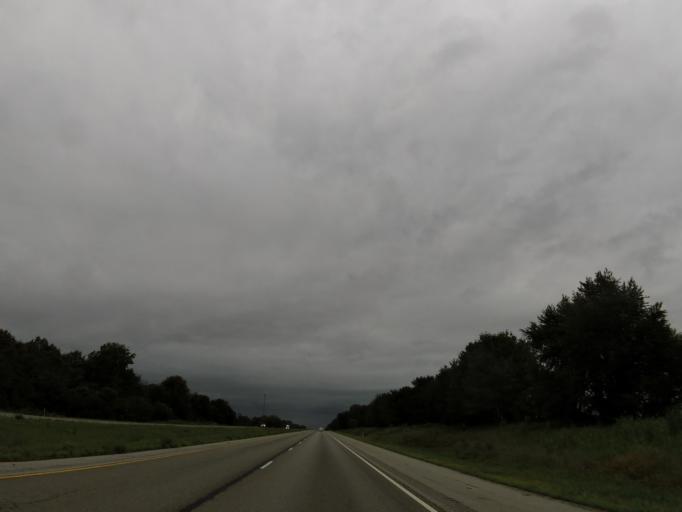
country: US
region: Illinois
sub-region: Massac County
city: Metropolis
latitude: 37.2313
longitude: -88.7090
